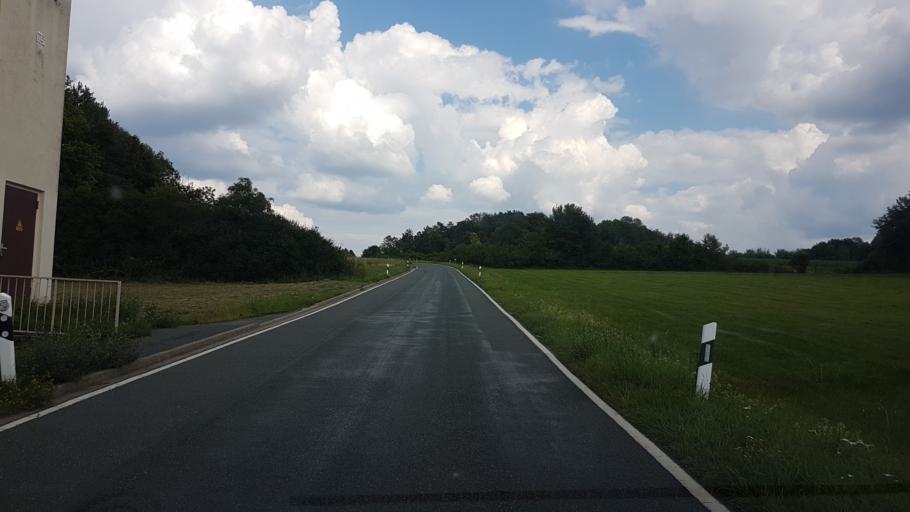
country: DE
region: Bavaria
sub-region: Upper Franconia
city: Gossweinstein
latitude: 49.7641
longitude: 11.3197
